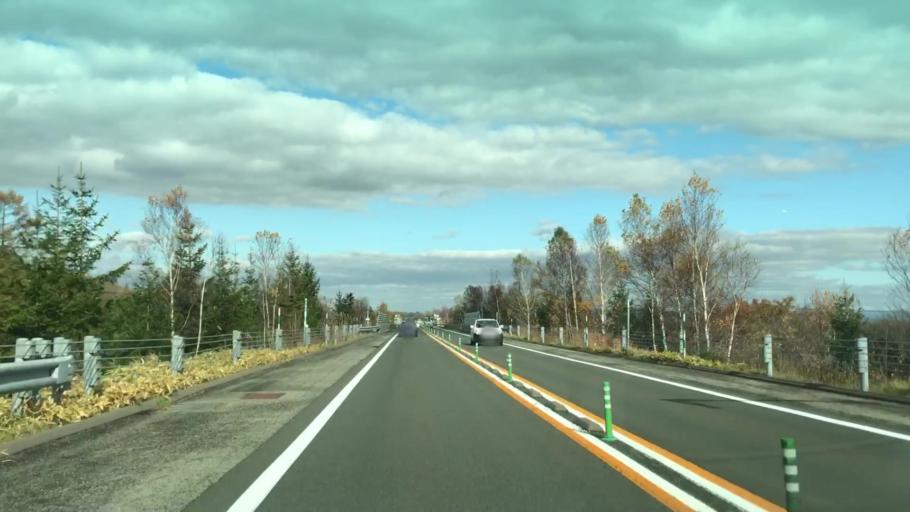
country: JP
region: Hokkaido
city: Chitose
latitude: 42.8736
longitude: 141.6149
